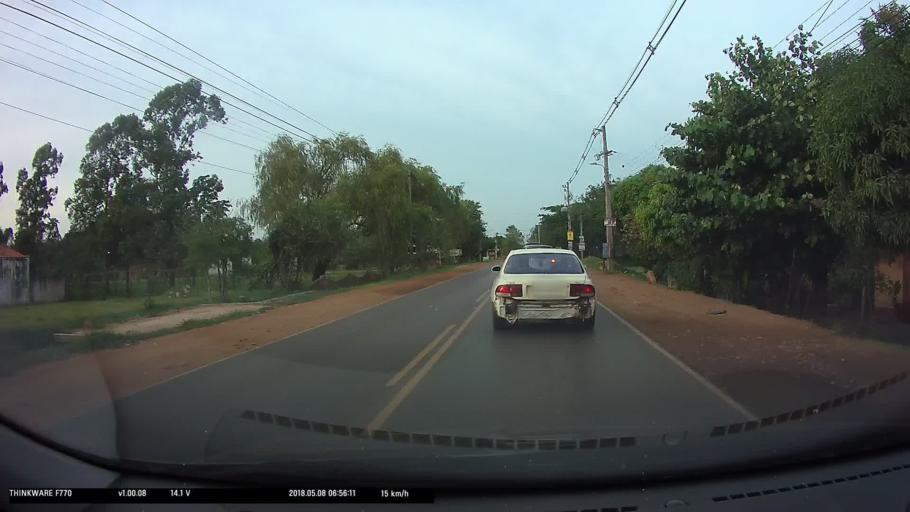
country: PY
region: Central
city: Limpio
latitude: -25.2394
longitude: -57.4745
